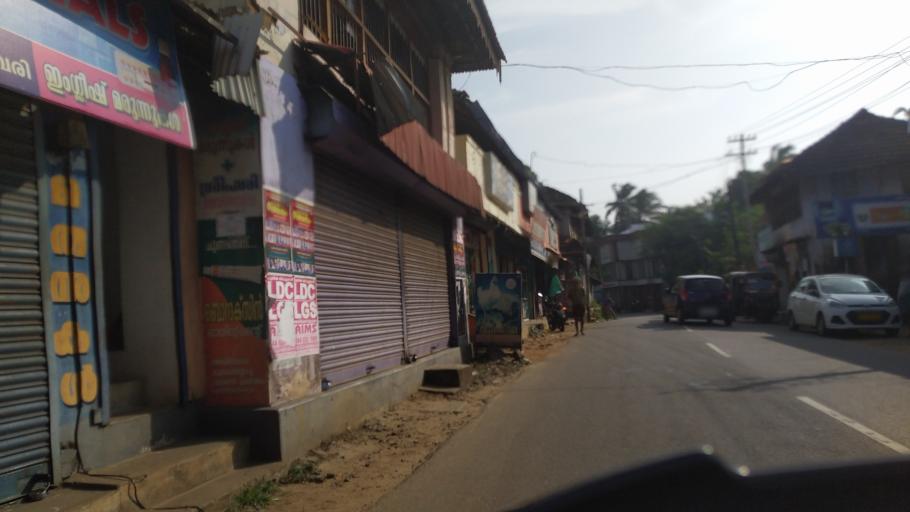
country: IN
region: Kerala
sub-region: Palakkad district
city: Palakkad
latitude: 10.5988
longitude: 76.5514
